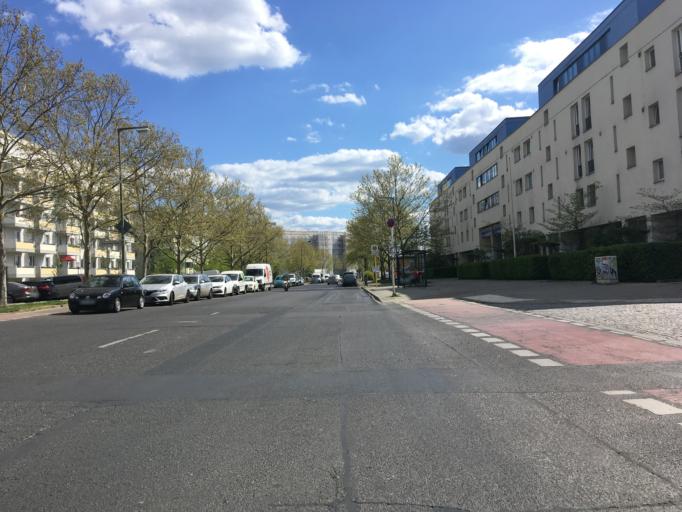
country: DE
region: Berlin
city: Hellersdorf
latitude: 52.5359
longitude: 13.6225
